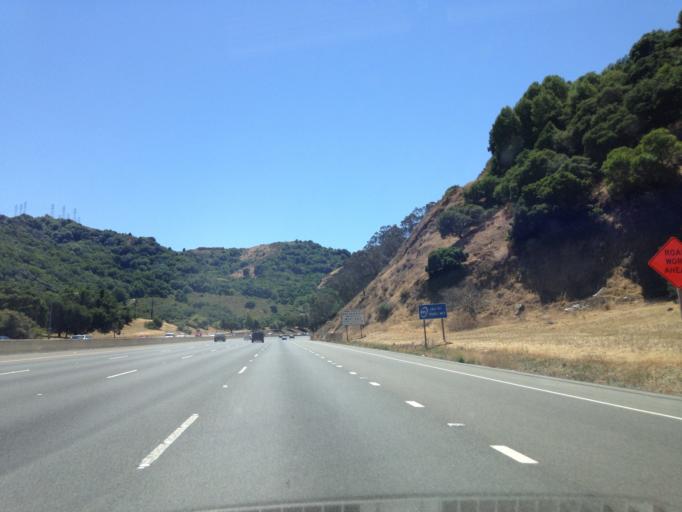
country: US
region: California
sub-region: Contra Costa County
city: Orinda
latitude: 37.8700
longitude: -122.1934
